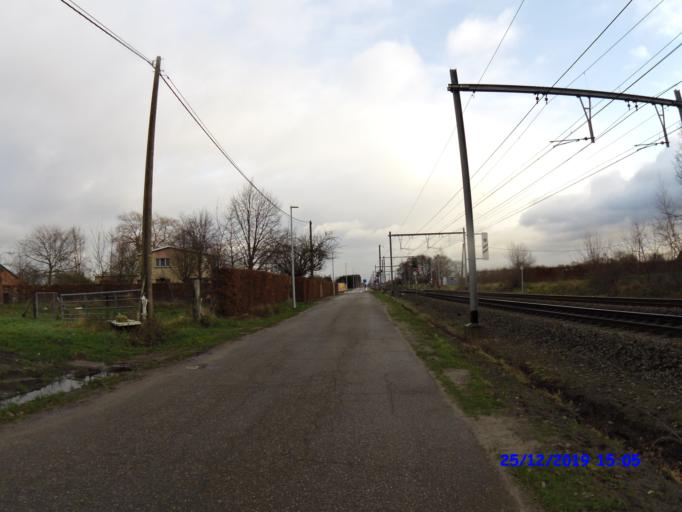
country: BE
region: Flanders
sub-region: Provincie Antwerpen
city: Geel
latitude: 51.1714
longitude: 4.9323
